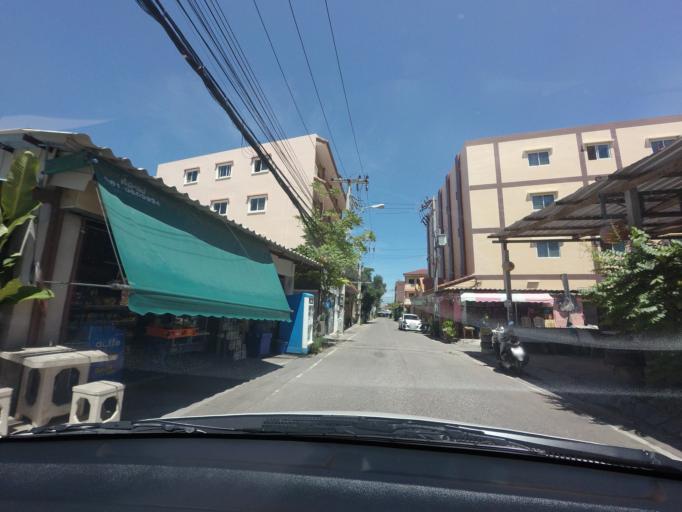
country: TH
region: Chon Buri
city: Phatthaya
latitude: 12.9541
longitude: 100.8972
